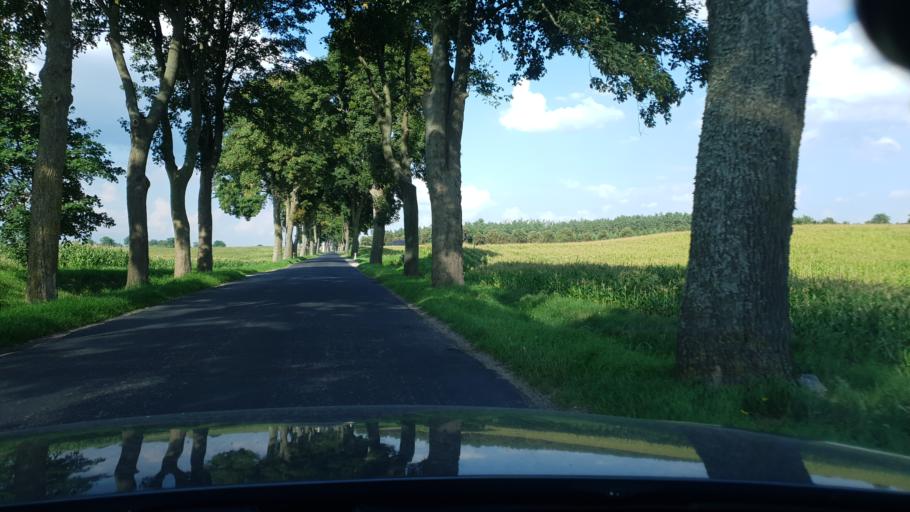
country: PL
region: Kujawsko-Pomorskie
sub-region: Powiat wabrzeski
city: Wabrzezno
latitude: 53.2578
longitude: 18.8903
